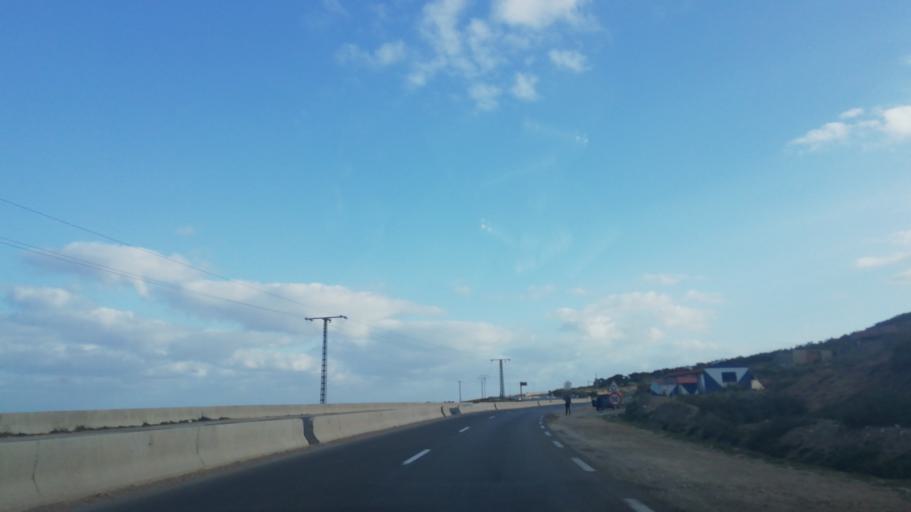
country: DZ
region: Mostaganem
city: Mostaganem
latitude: 36.1013
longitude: 0.2130
